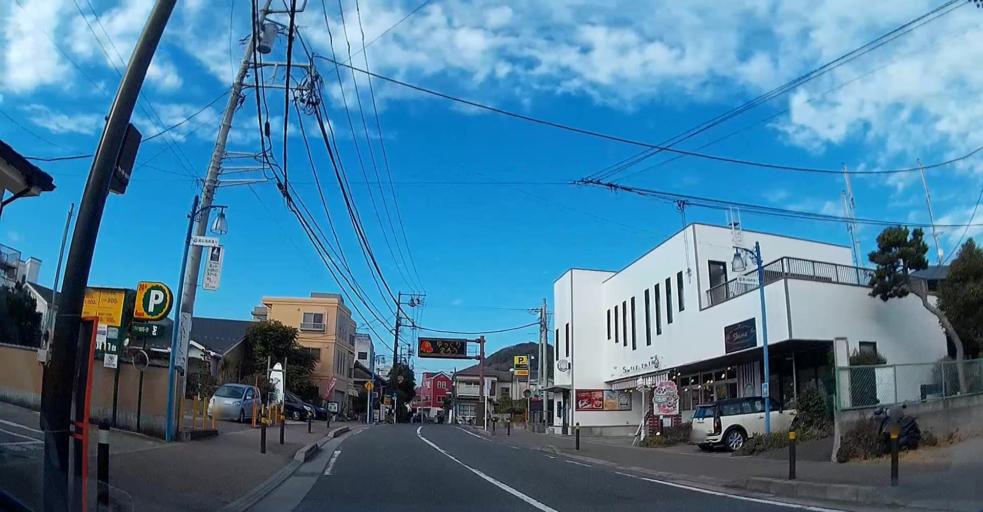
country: JP
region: Kanagawa
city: Hayama
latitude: 35.2757
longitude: 139.5732
